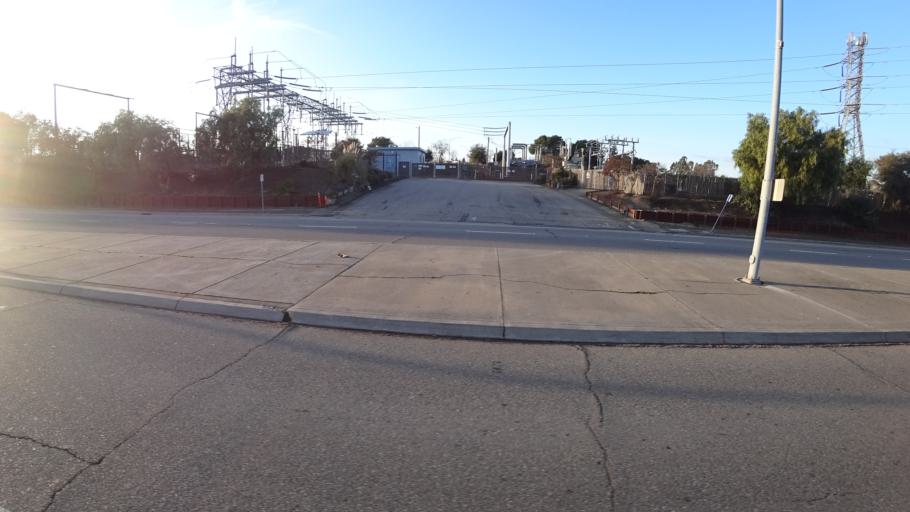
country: US
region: California
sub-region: Alameda County
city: Fairview
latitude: 37.6911
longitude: -122.0603
